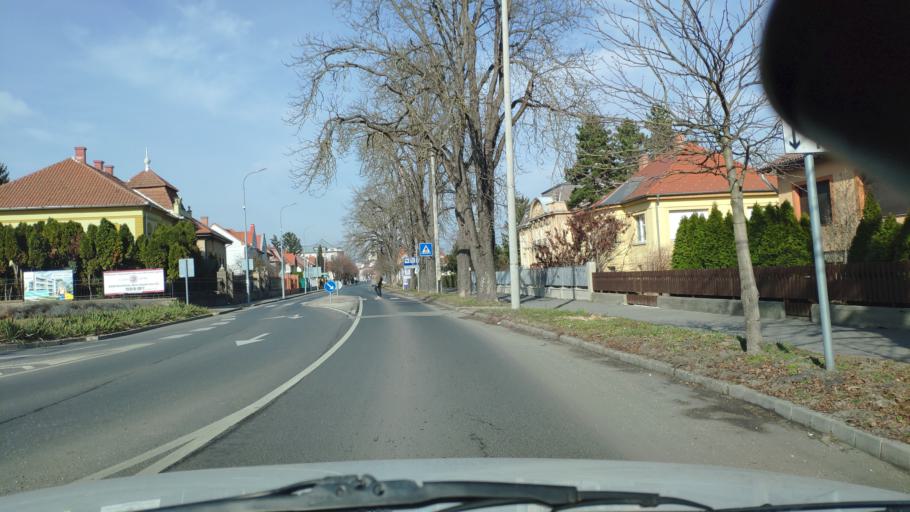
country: HU
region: Zala
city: Keszthely
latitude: 46.7579
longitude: 17.2416
